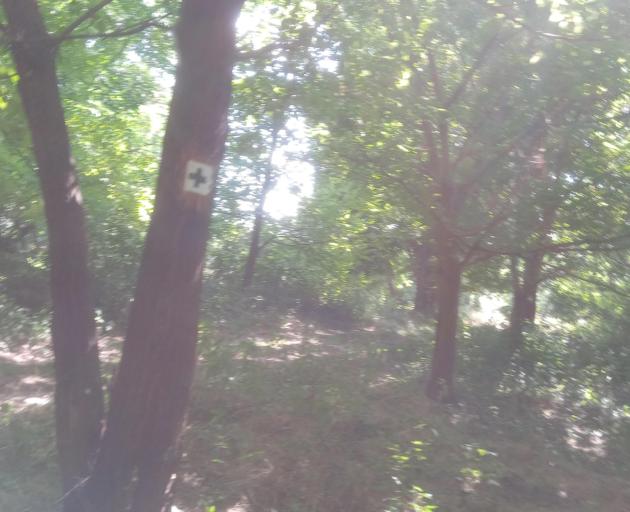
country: HU
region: Fejer
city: Pakozd
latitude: 47.2308
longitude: 18.4908
